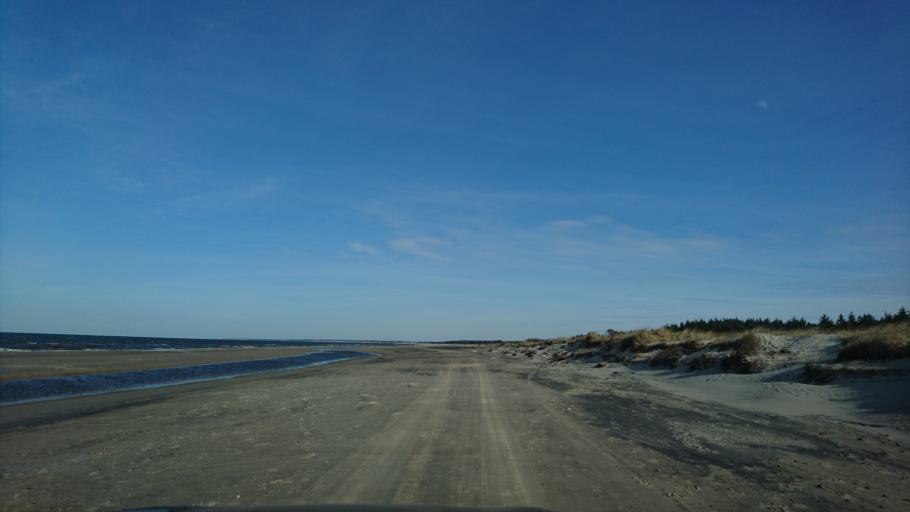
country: DK
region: North Denmark
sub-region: Hjorring Kommune
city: Hirtshals
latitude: 57.5909
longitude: 10.0549
